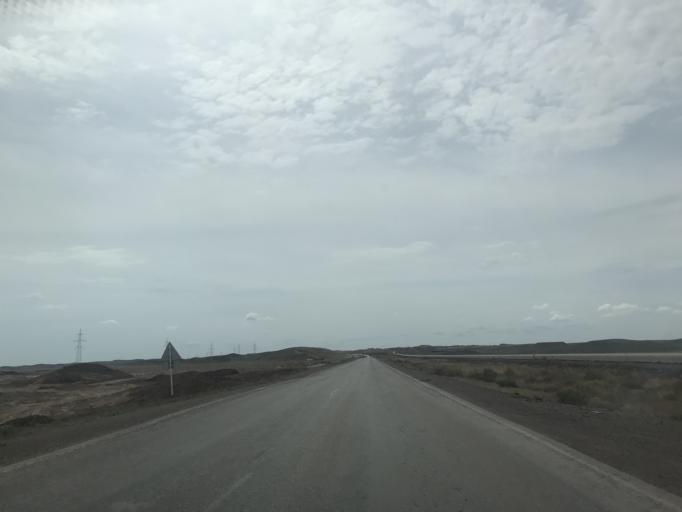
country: KZ
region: Zhambyl
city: Mynaral
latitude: 45.3816
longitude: 73.6519
